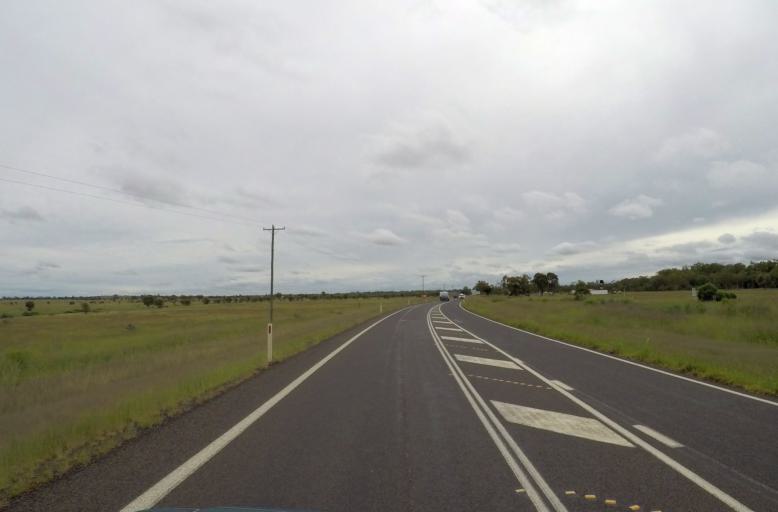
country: AU
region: Queensland
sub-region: Maranoa
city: Roma
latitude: -26.5310
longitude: 148.7796
